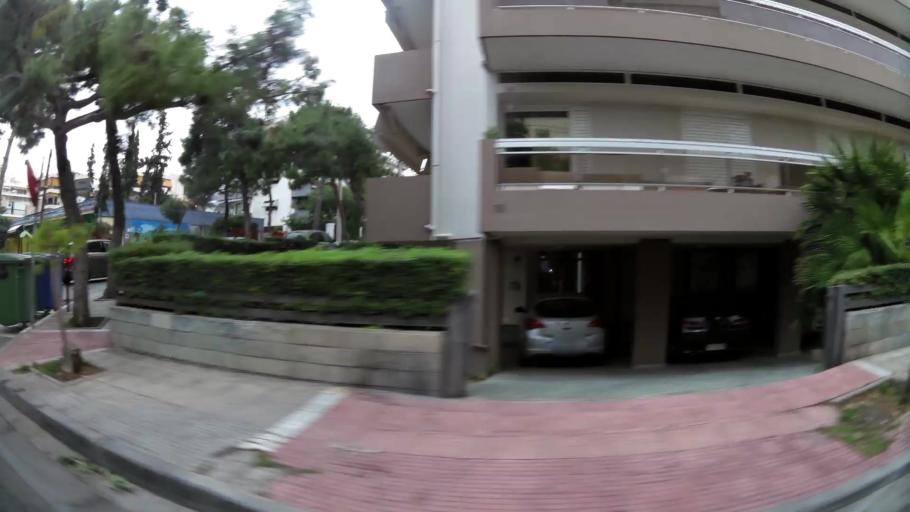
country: GR
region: Attica
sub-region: Nomarchia Athinas
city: Alimos
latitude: 37.9104
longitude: 23.7161
